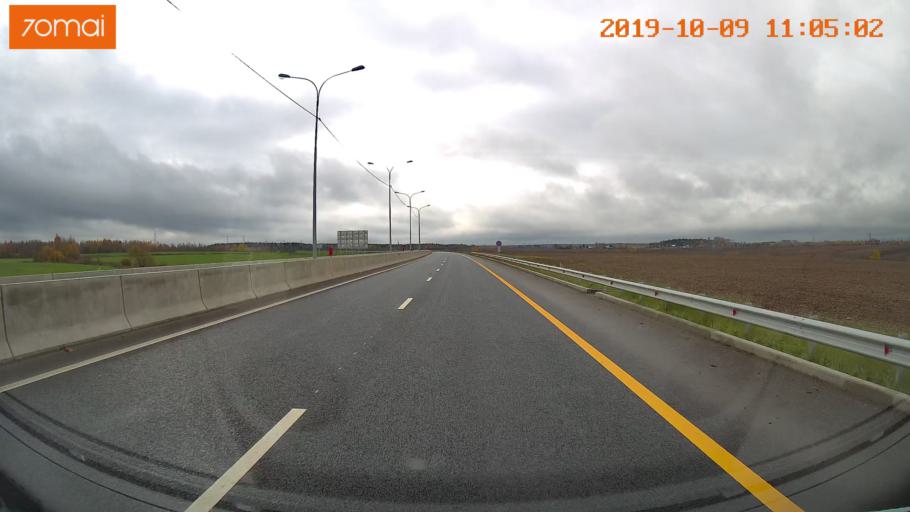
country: RU
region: Vologda
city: Molochnoye
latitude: 59.2050
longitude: 39.7607
